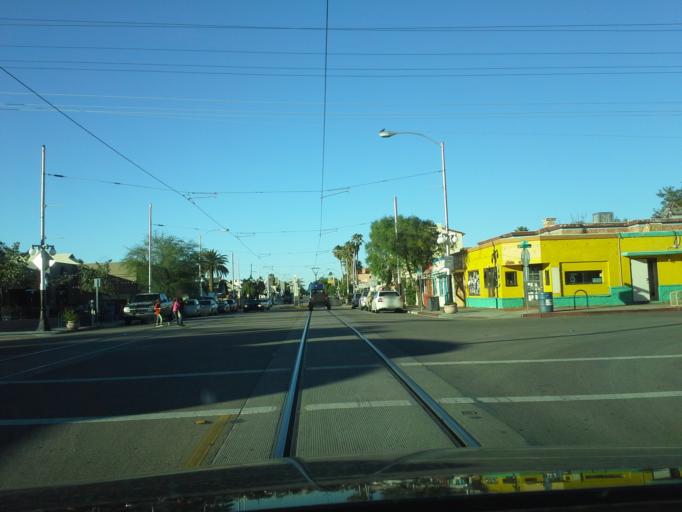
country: US
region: Arizona
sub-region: Pima County
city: South Tucson
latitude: 32.2289
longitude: -110.9656
